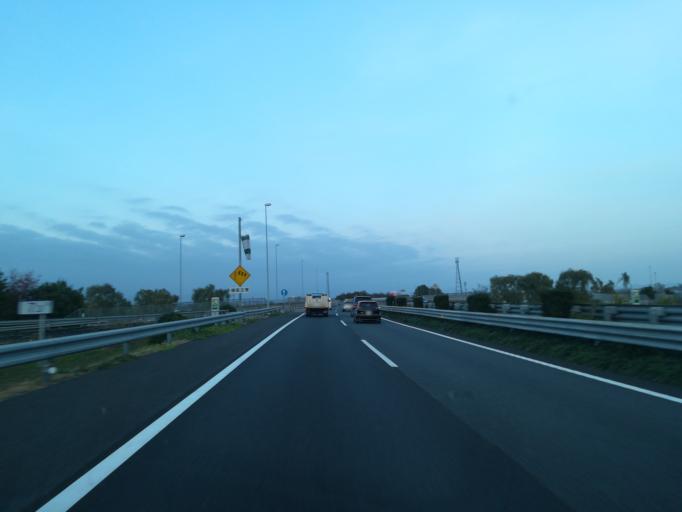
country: JP
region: Gunma
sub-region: Sawa-gun
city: Tamamura
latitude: 36.3473
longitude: 139.1421
